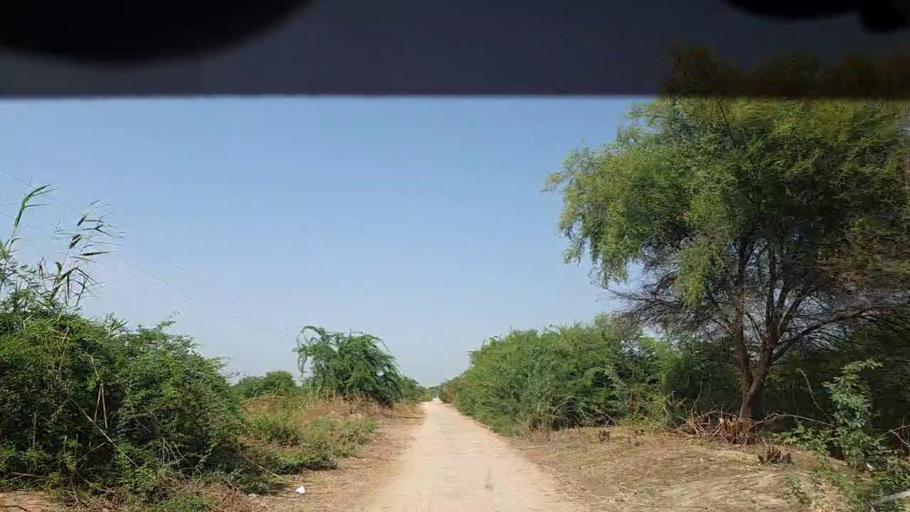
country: PK
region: Sindh
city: Badin
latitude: 24.4642
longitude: 68.7796
